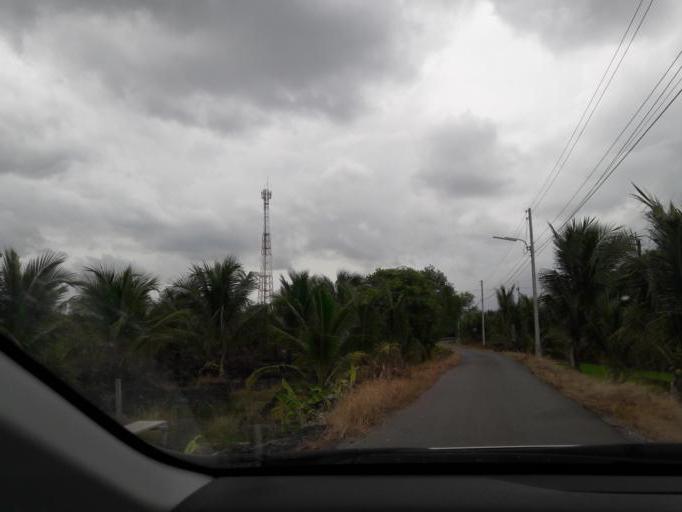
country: TH
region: Samut Sakhon
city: Ban Phaeo
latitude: 13.5952
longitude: 100.0267
